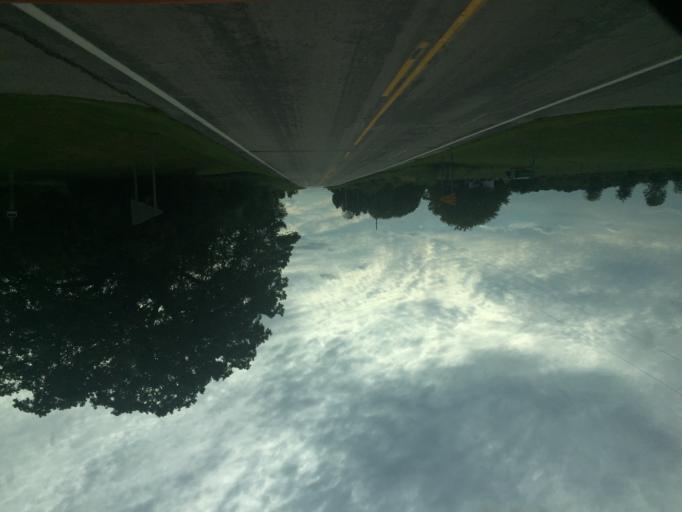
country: US
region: Minnesota
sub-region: Olmsted County
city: Rochester
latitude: 43.9640
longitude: -92.5283
